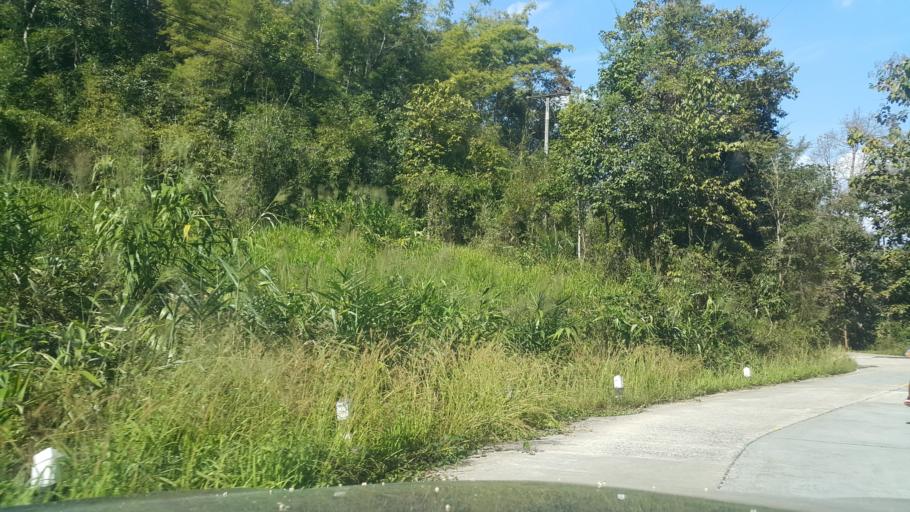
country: TH
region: Chiang Mai
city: Samoeng
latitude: 18.9231
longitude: 98.6735
